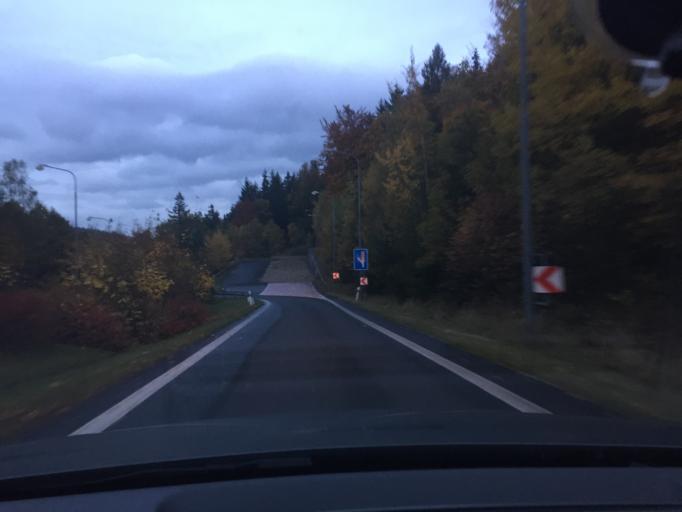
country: CZ
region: Ustecky
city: Dubi
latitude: 50.6897
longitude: 13.7761
